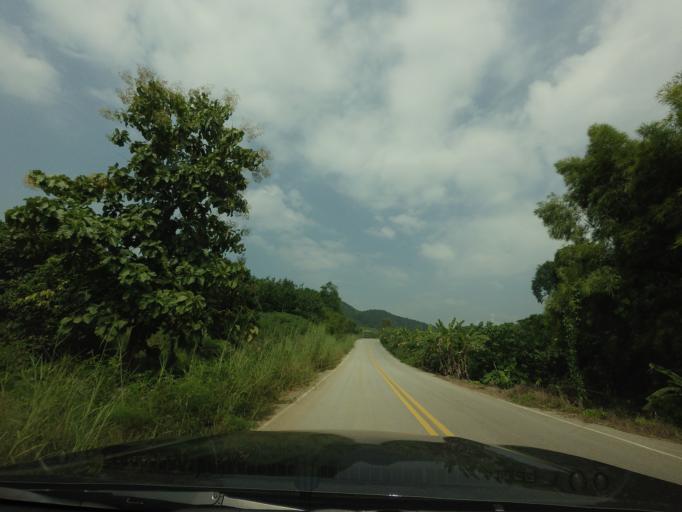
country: LA
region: Xiagnabouli
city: Muang Kenthao
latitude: 17.7239
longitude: 101.4871
